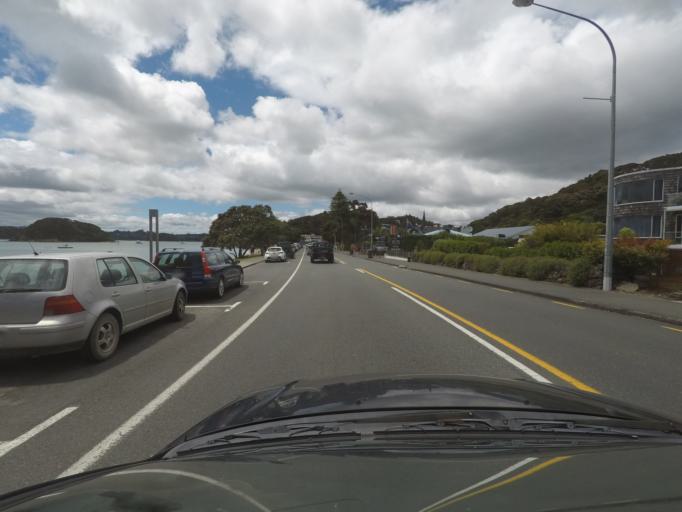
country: NZ
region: Northland
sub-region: Far North District
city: Paihia
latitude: -35.2826
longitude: 174.0931
